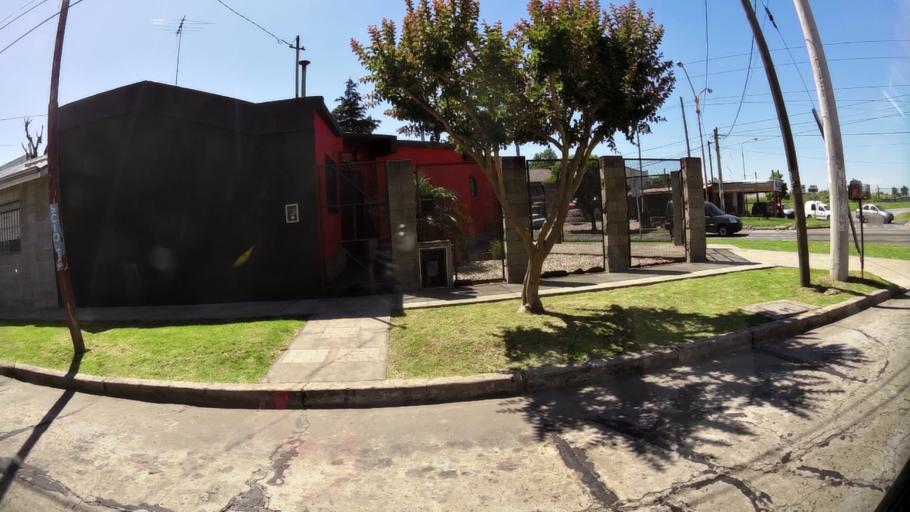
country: AR
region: Buenos Aires
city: Ituzaingo
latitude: -34.6615
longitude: -58.6423
